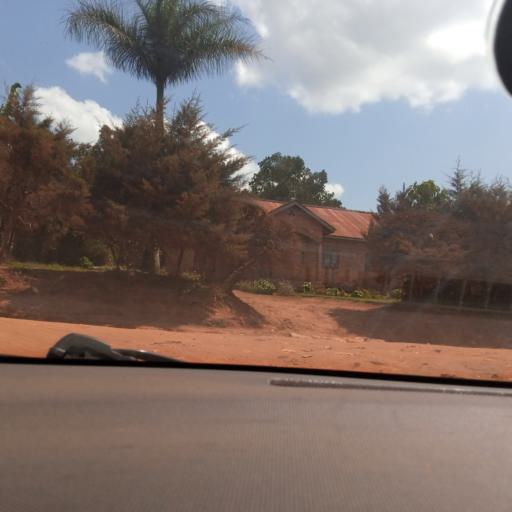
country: UG
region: Central Region
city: Masaka
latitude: -0.3310
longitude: 31.7417
